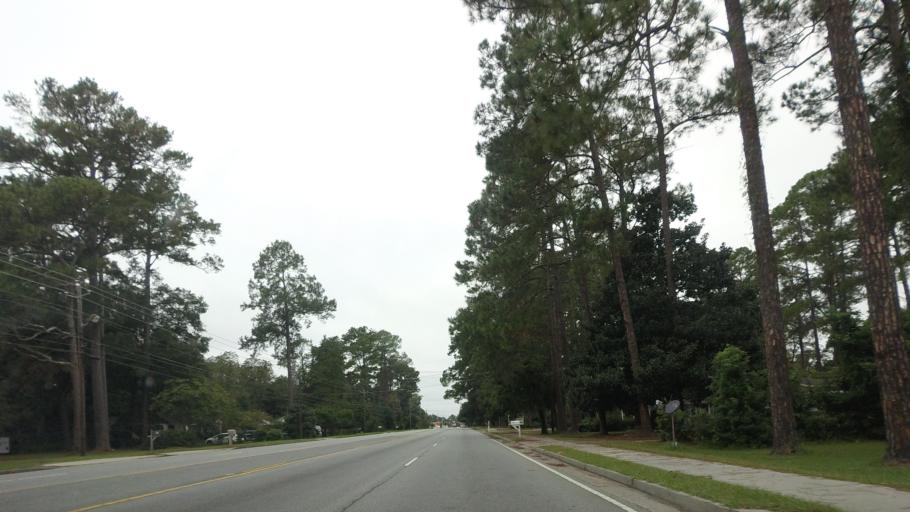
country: US
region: Georgia
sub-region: Lowndes County
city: Valdosta
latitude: 30.8572
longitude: -83.2736
